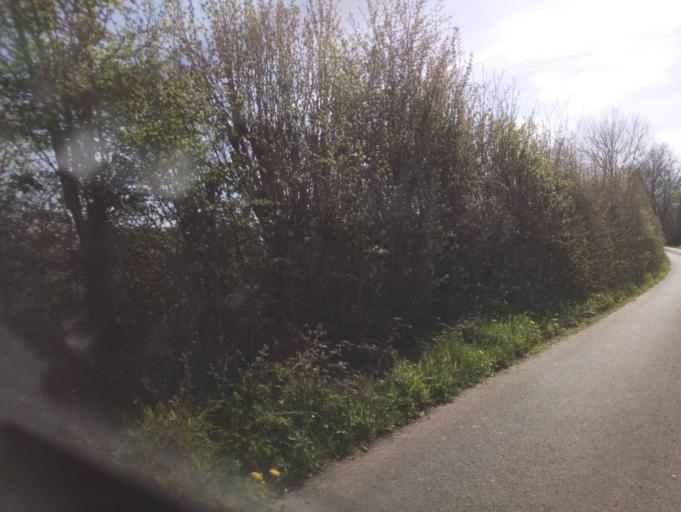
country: GB
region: Wales
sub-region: Monmouthshire
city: Llangwm
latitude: 51.7585
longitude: -2.8269
